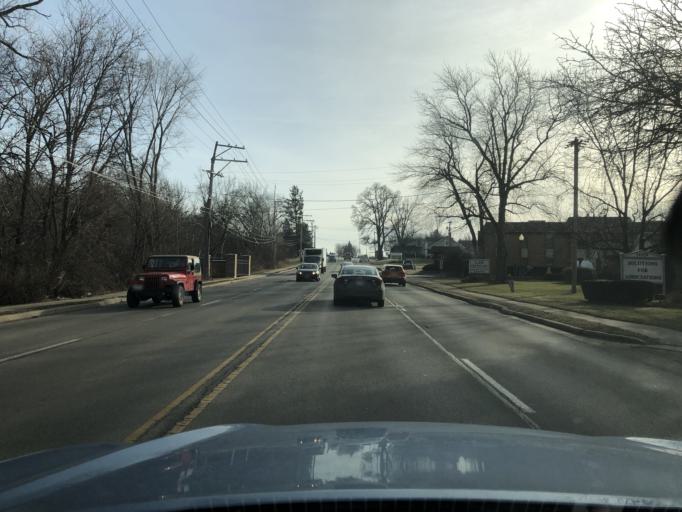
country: US
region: Illinois
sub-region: DuPage County
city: Bloomingdale
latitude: 41.9612
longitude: -88.0819
